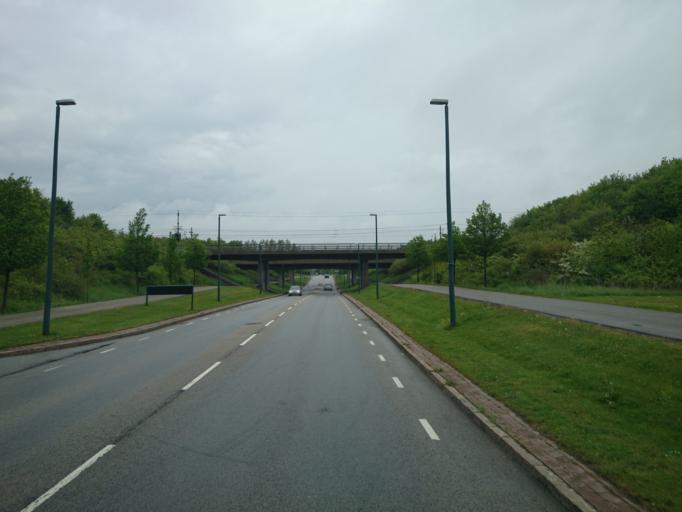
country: SE
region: Skane
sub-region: Malmo
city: Bunkeflostrand
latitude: 55.5641
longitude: 12.9201
